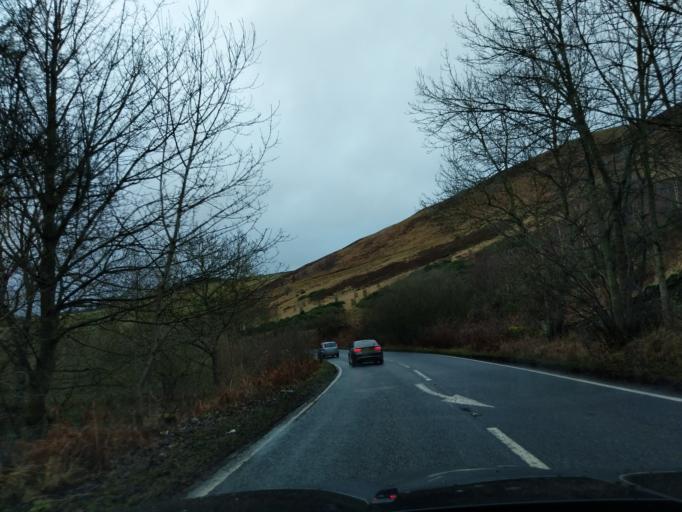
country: GB
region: Scotland
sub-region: The Scottish Borders
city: Galashiels
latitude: 55.6626
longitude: -2.8606
